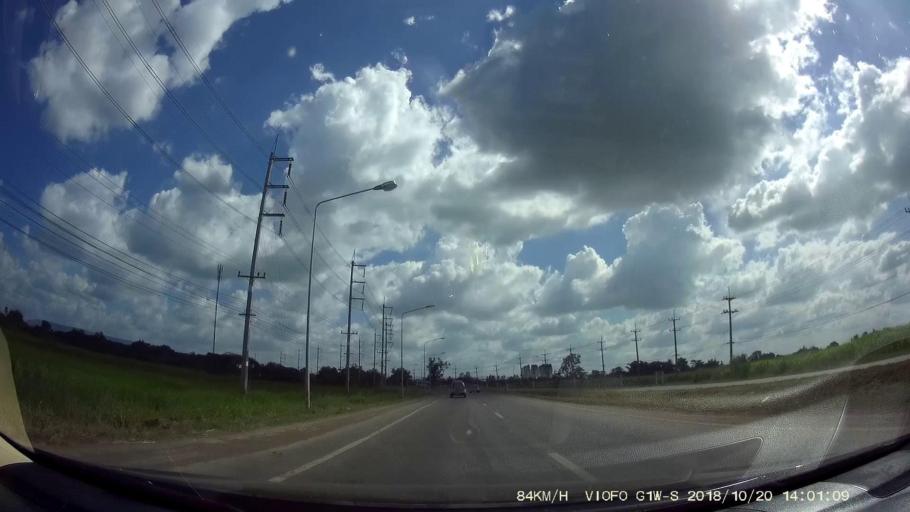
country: TH
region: Khon Kaen
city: Chum Phae
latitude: 16.5053
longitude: 102.1188
